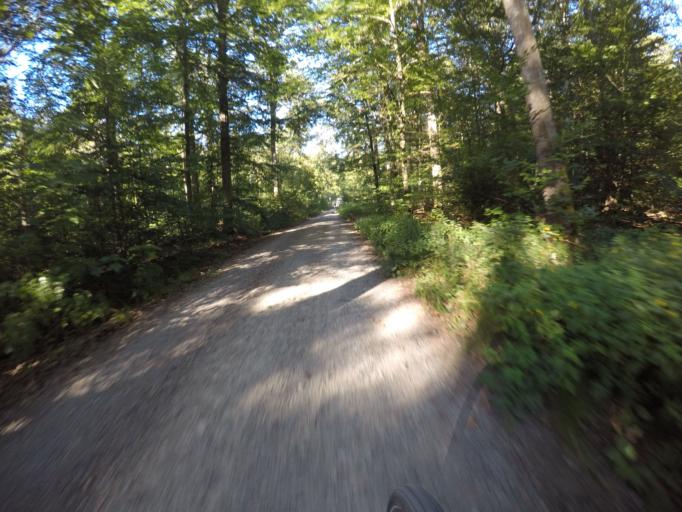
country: DE
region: Baden-Wuerttemberg
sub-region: Regierungsbezirk Stuttgart
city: Nufringen
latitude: 48.6044
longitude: 8.9191
